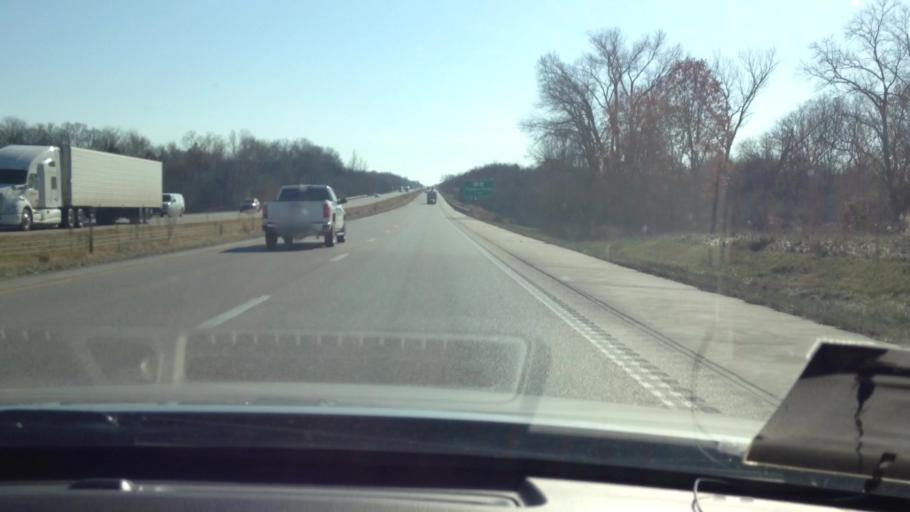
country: US
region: Missouri
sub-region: Platte County
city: Platte City
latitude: 39.4690
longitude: -94.7878
